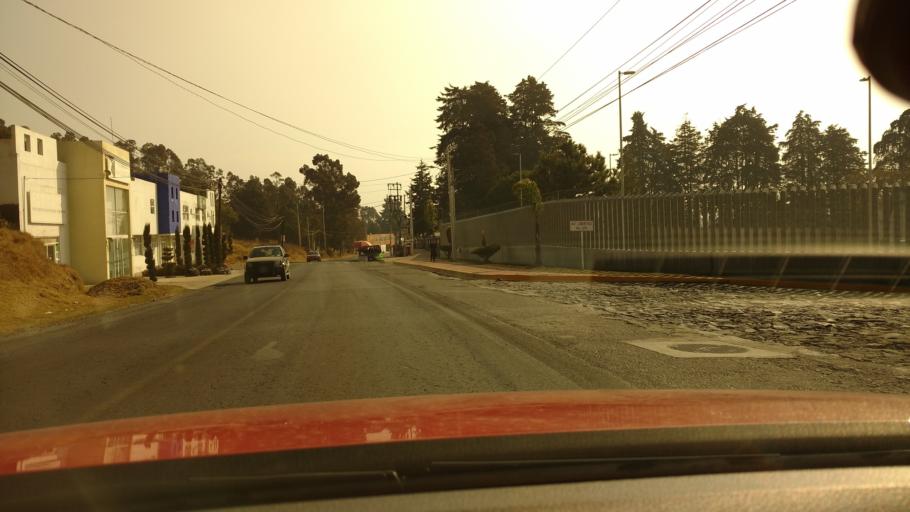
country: MX
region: Morelos
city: Chapultepec
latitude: 19.2032
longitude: -99.5557
